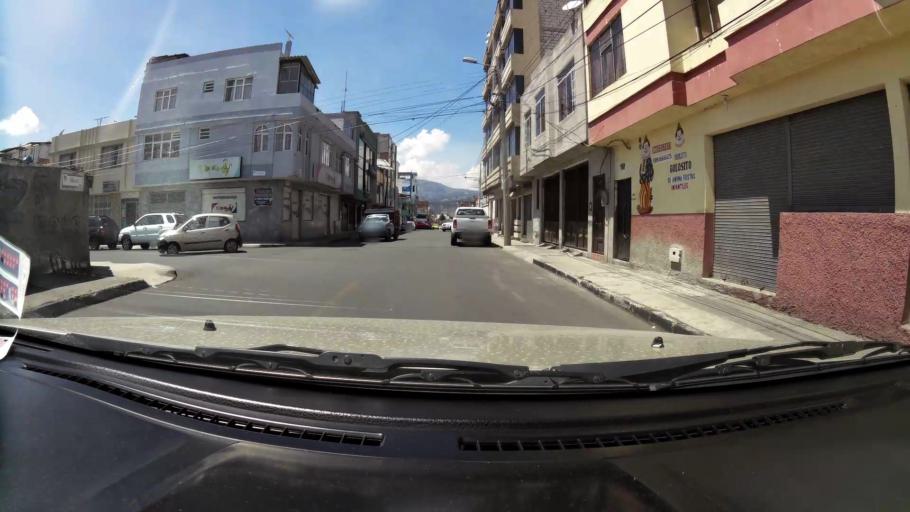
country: EC
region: Chimborazo
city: Riobamba
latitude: -1.6636
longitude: -78.6536
